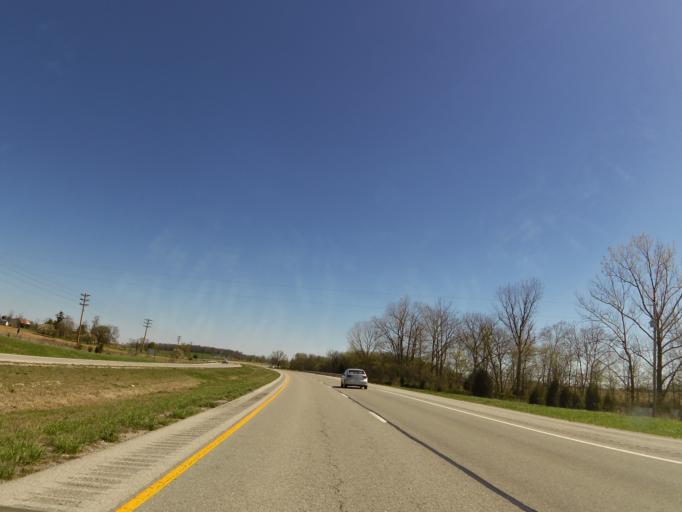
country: US
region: Kentucky
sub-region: Logan County
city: Auburn
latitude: 36.8714
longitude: -86.6880
